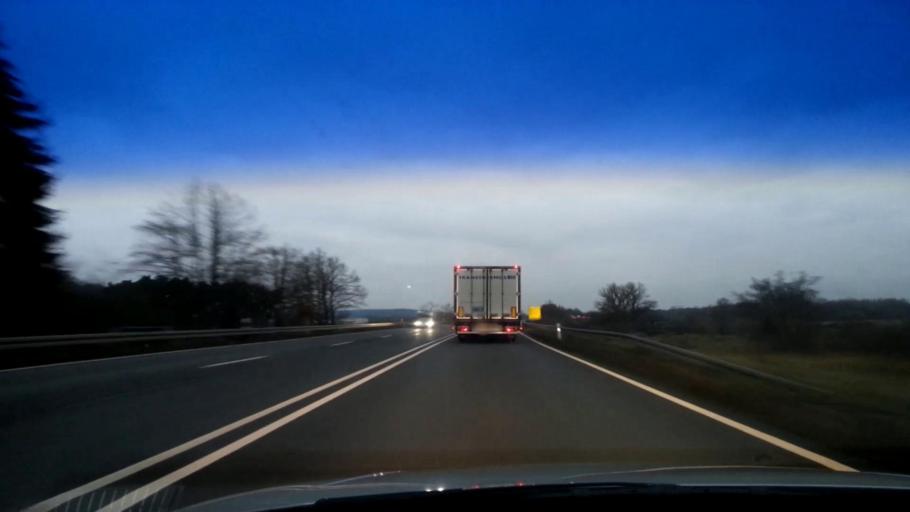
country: DE
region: Bavaria
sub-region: Upper Franconia
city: Strullendorf
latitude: 49.8236
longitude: 10.9548
